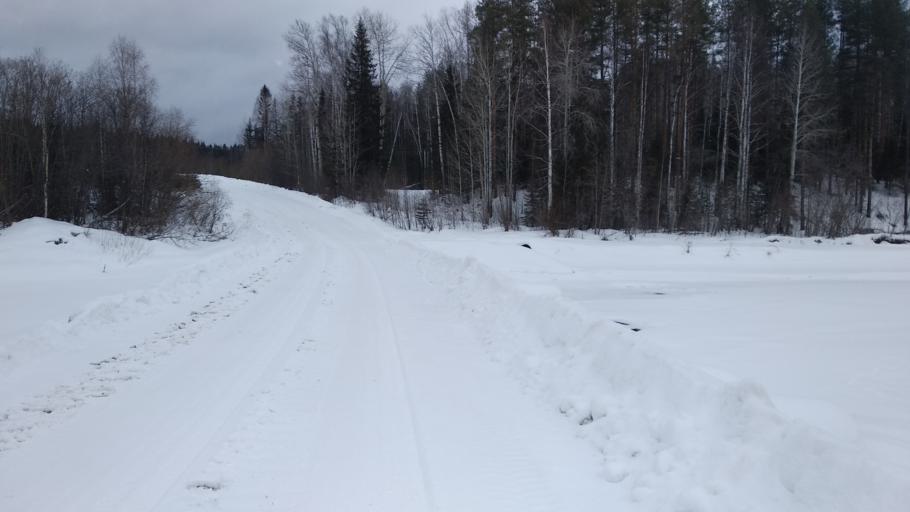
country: RU
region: Sverdlovsk
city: Rudnichnyy
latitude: 59.4413
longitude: 60.2019
